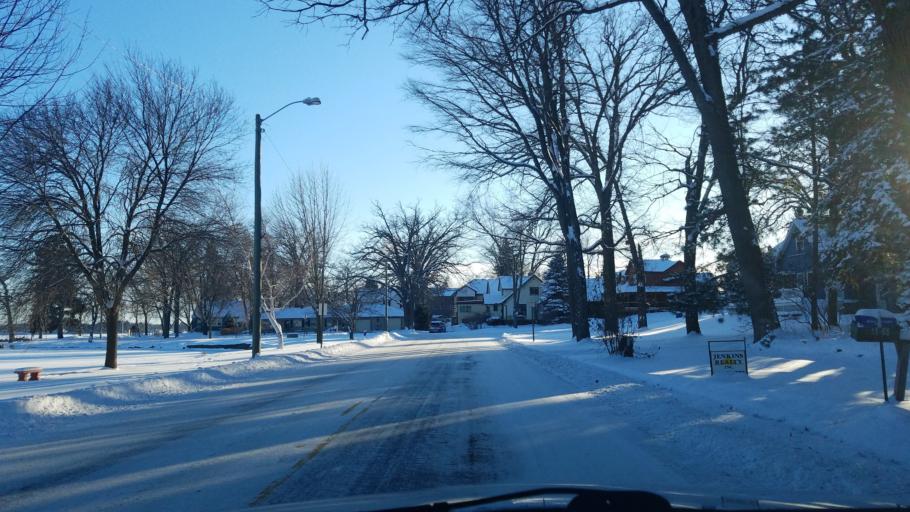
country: US
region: Wisconsin
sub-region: Barron County
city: Rice Lake
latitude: 45.5061
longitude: -91.7315
